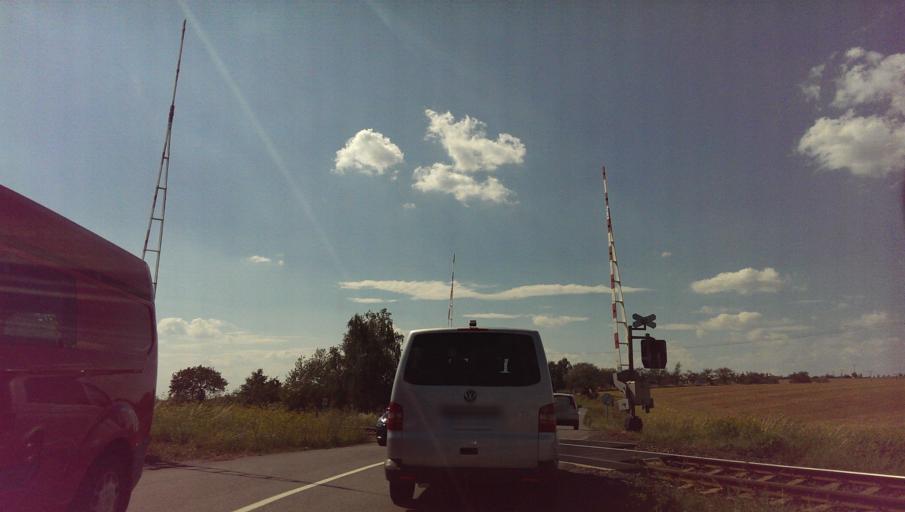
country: CZ
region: Zlin
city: Kelc
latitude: 49.4424
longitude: 17.8227
